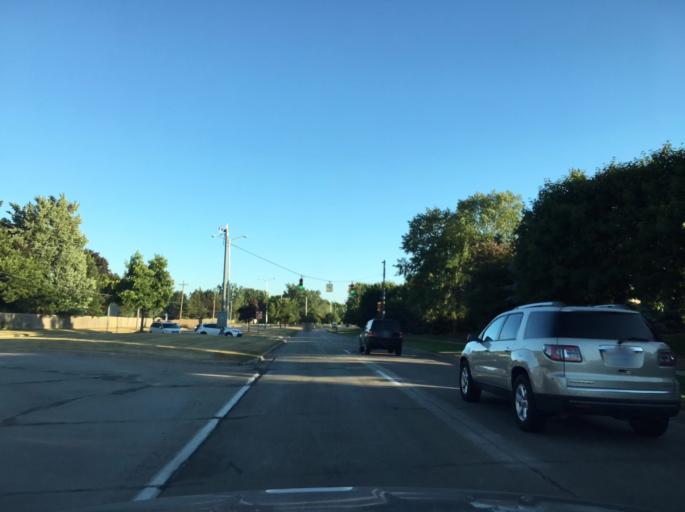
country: US
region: Michigan
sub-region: Macomb County
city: Sterling Heights
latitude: 42.5915
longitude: -82.9915
